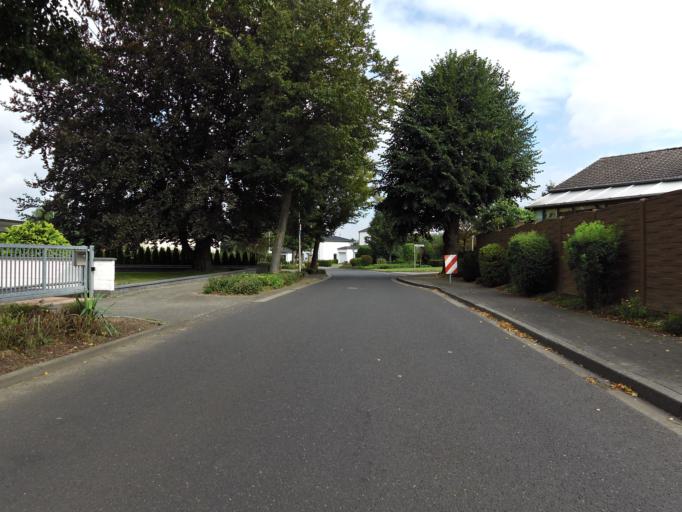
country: DE
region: North Rhine-Westphalia
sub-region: Regierungsbezirk Koln
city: Ubach-Palenberg
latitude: 50.9491
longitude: 6.0825
